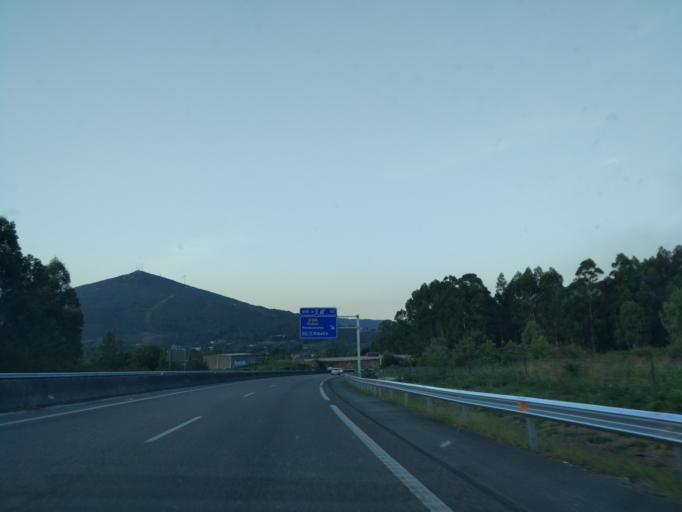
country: ES
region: Galicia
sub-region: Provincia da Coruna
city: Padron
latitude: 42.7244
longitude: -8.6397
